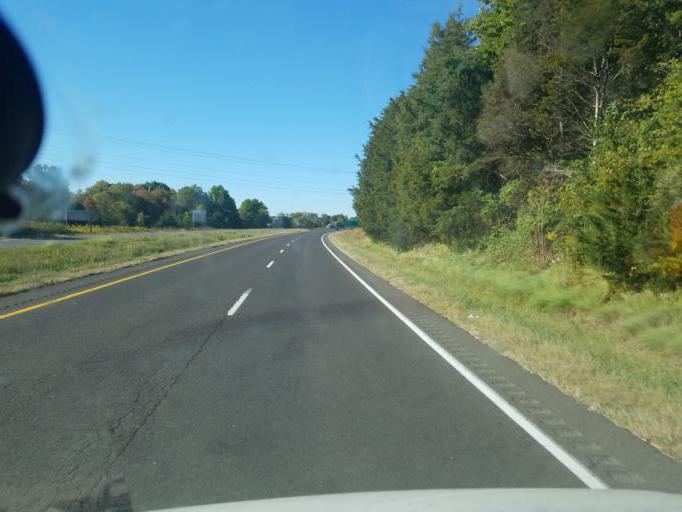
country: US
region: Virginia
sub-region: Culpeper County
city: Culpeper
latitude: 38.4864
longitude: -77.9386
